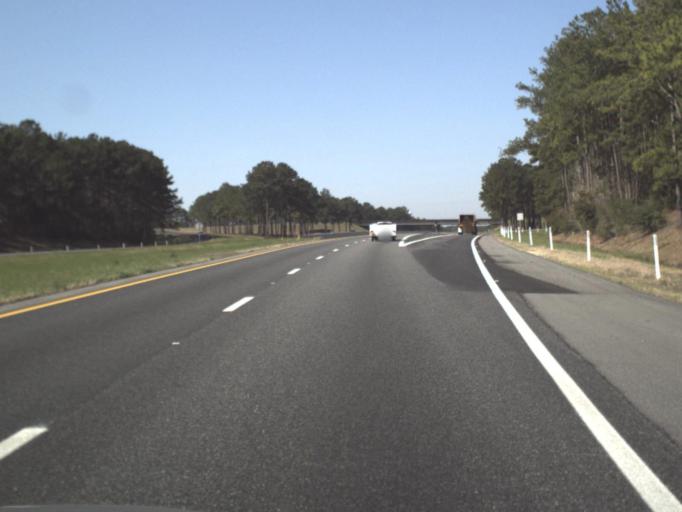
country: US
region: Florida
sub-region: Gadsden County
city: Chattahoochee
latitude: 30.6183
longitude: -84.8169
